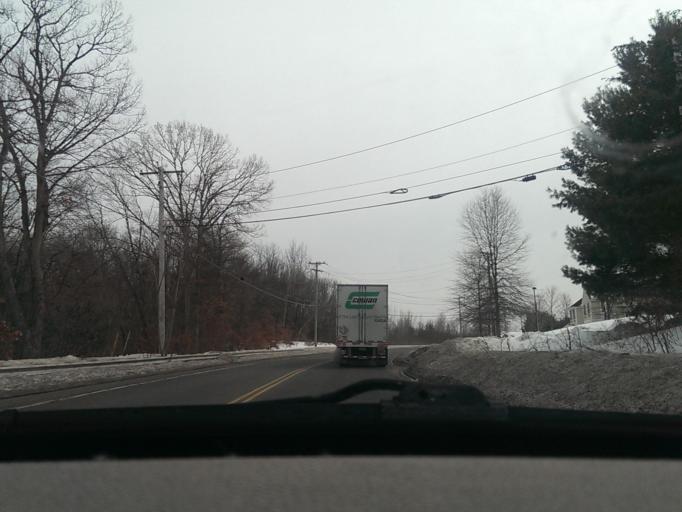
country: US
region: Massachusetts
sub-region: Hampden County
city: East Longmeadow
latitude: 42.0558
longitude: -72.5345
